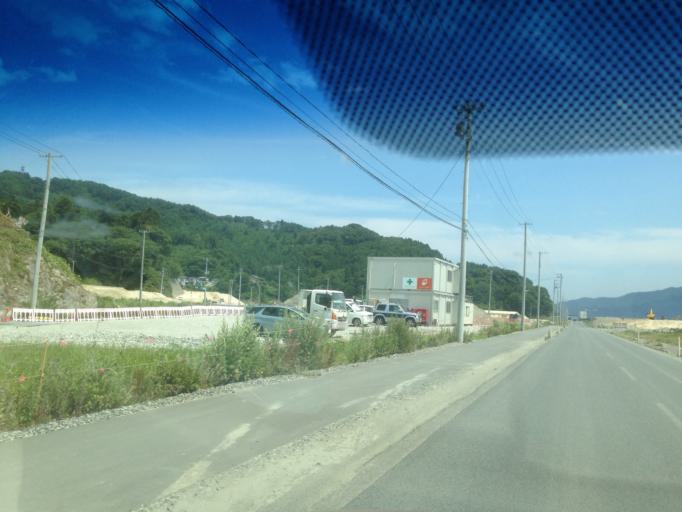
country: JP
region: Iwate
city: Otsuchi
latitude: 39.3593
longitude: 141.9140
